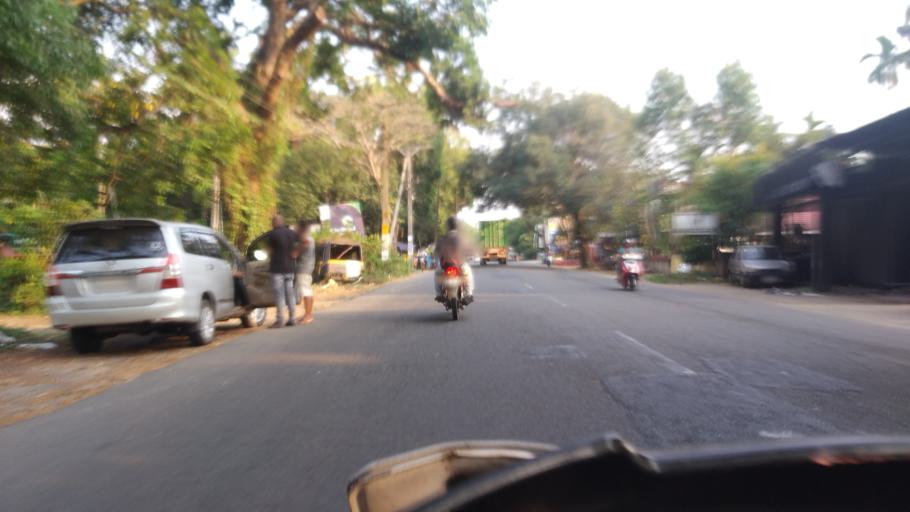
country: IN
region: Kerala
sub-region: Thrissur District
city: Irinjalakuda
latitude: 10.3293
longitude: 76.1418
